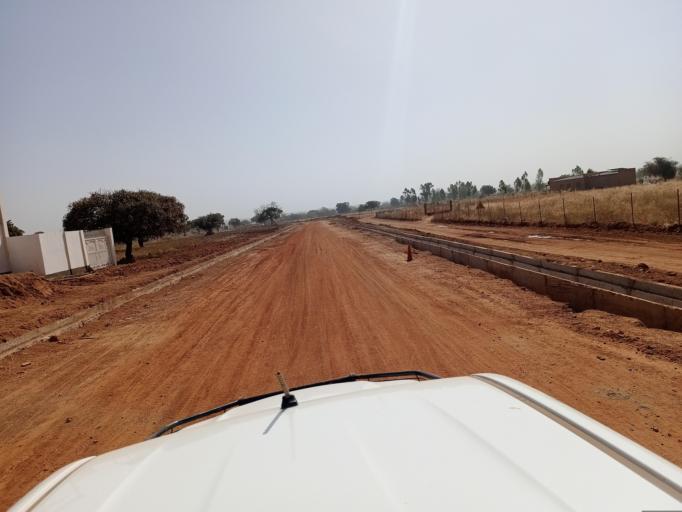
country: BF
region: Centre-Est
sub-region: Province du Boulgou
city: Garango
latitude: 11.5013
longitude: -0.5140
